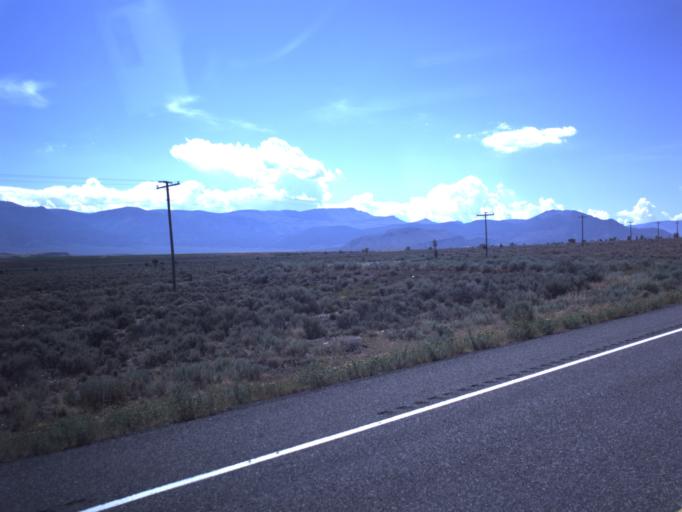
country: US
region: Utah
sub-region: Piute County
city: Junction
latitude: 38.3992
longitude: -112.2311
